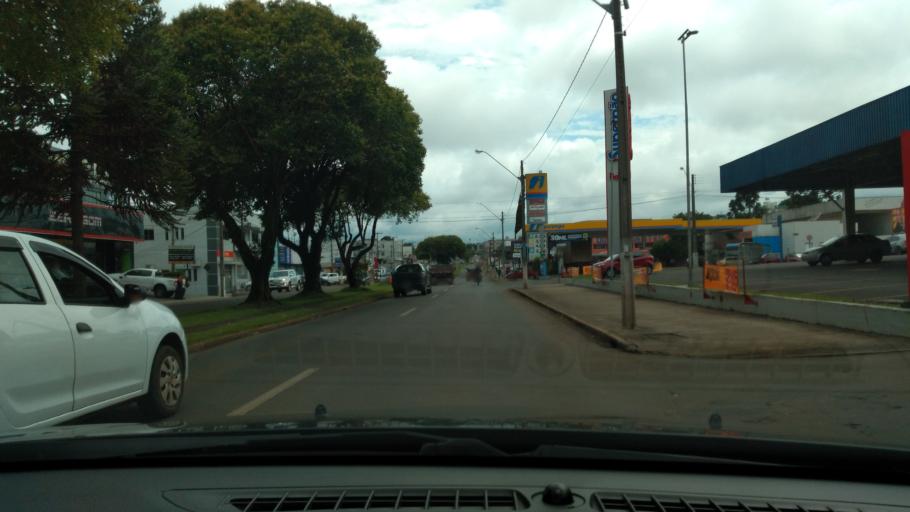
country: BR
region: Parana
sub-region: Guarapuava
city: Guarapuava
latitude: -25.3877
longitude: -51.4746
